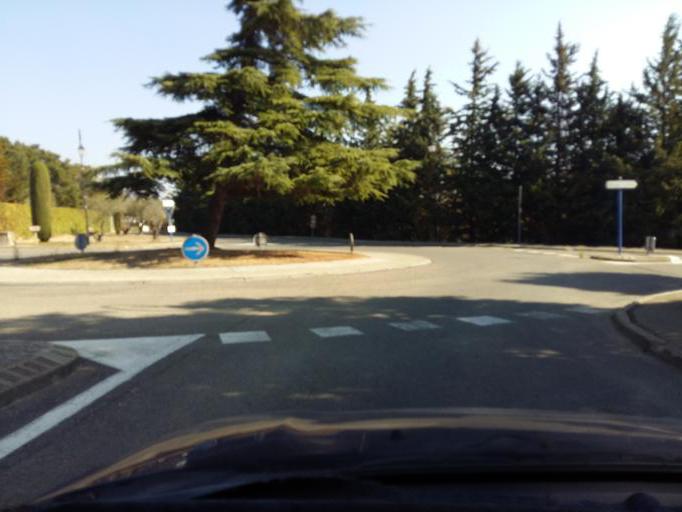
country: FR
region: Provence-Alpes-Cote d'Azur
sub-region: Departement du Vaucluse
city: Serignan-du-Comtat
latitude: 44.1924
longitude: 4.8454
